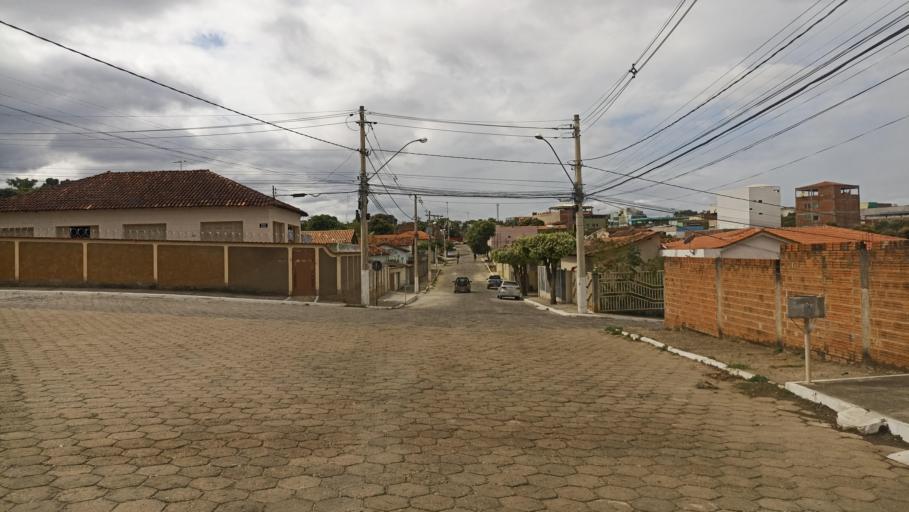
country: BR
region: Minas Gerais
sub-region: Aracuai
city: Aracuai
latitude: -16.8500
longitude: -42.0694
